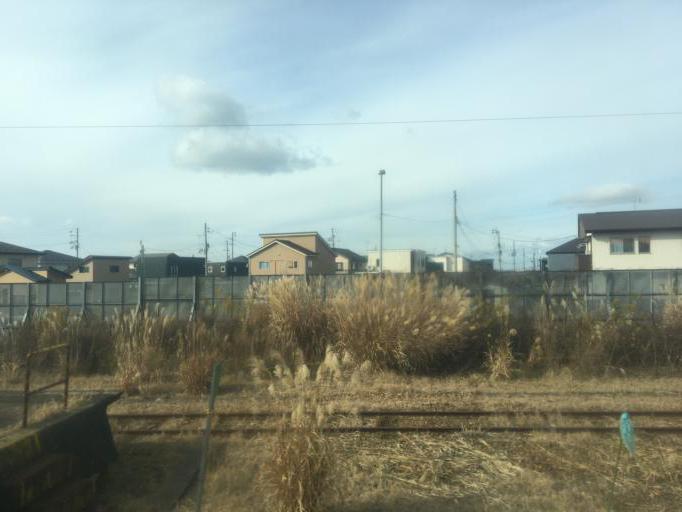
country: JP
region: Akita
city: Tenno
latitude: 39.8722
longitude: 140.0633
